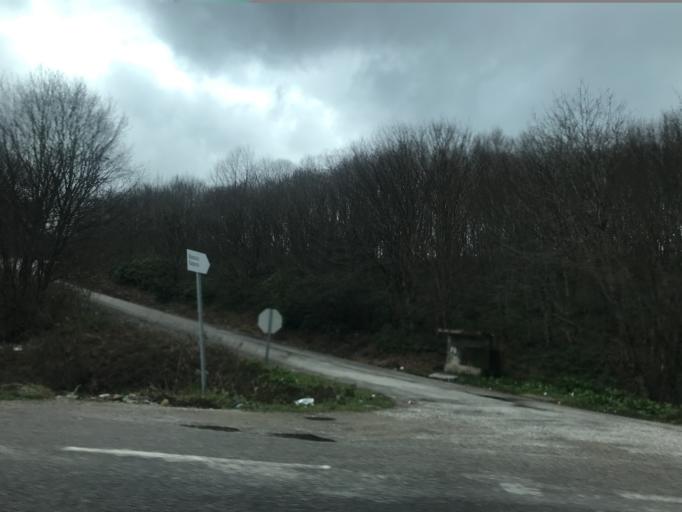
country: TR
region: Bartin
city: Amasra
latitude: 41.7122
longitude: 32.3919
